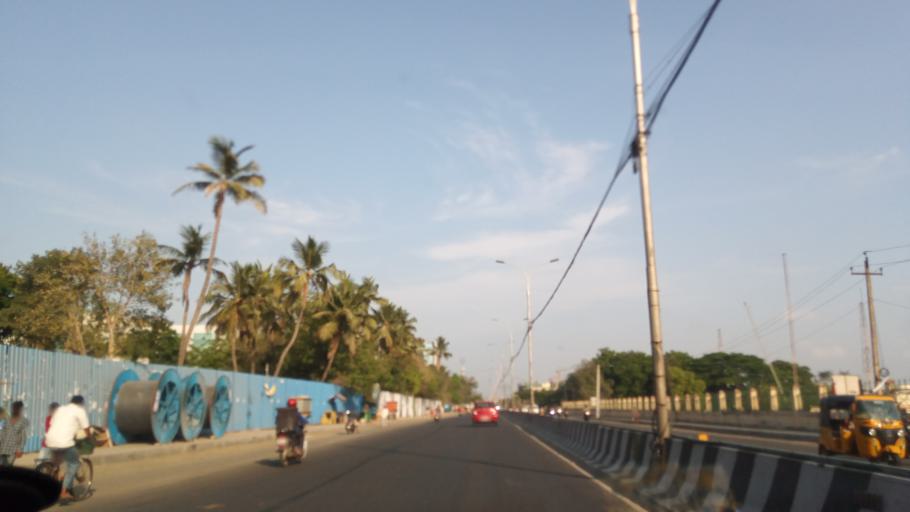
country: IN
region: Tamil Nadu
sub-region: Thiruvallur
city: Porur
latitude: 13.0311
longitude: 80.1656
